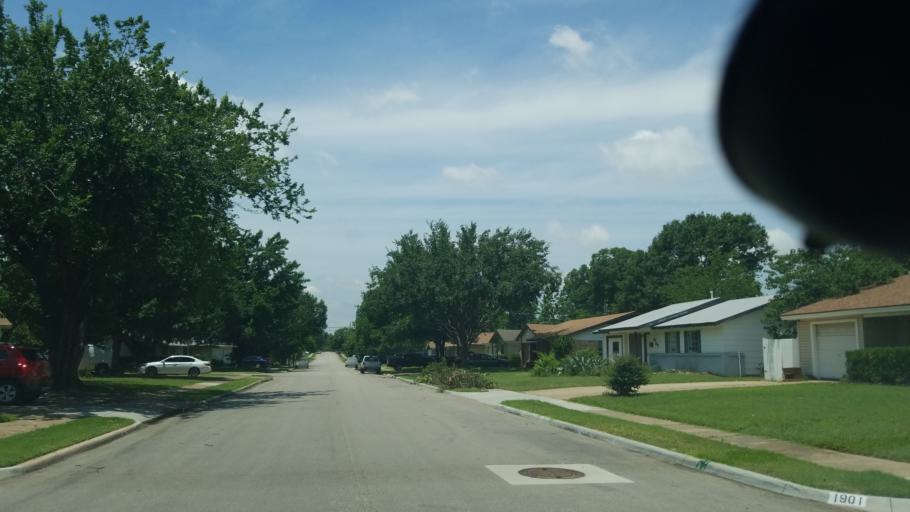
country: US
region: Texas
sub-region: Dallas County
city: Irving
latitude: 32.8464
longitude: -96.9699
